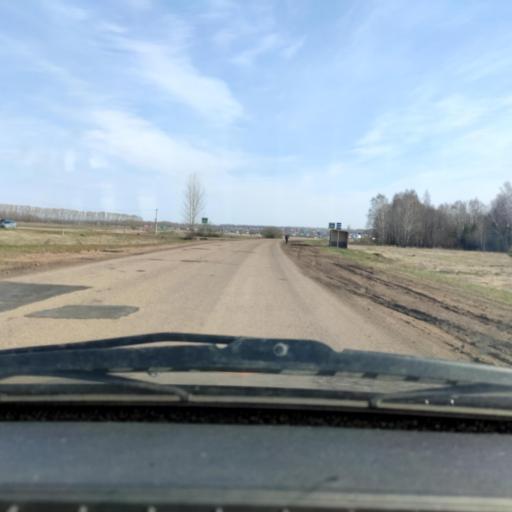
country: RU
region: Bashkortostan
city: Asanovo
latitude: 54.8020
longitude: 55.5366
